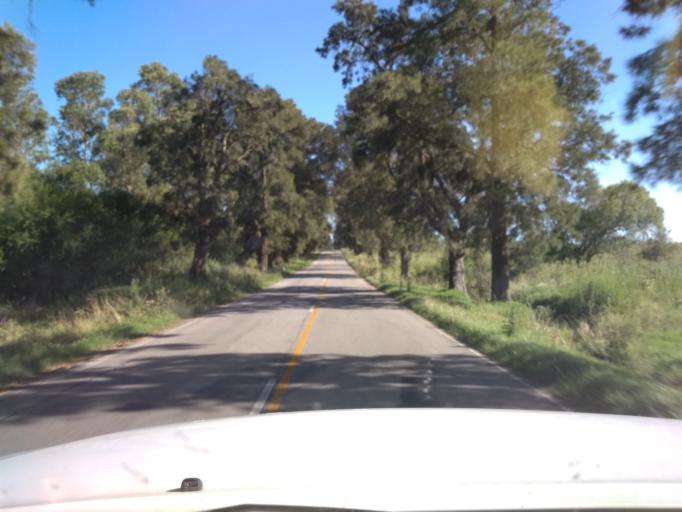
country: UY
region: Canelones
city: San Bautista
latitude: -34.3732
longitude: -55.9595
